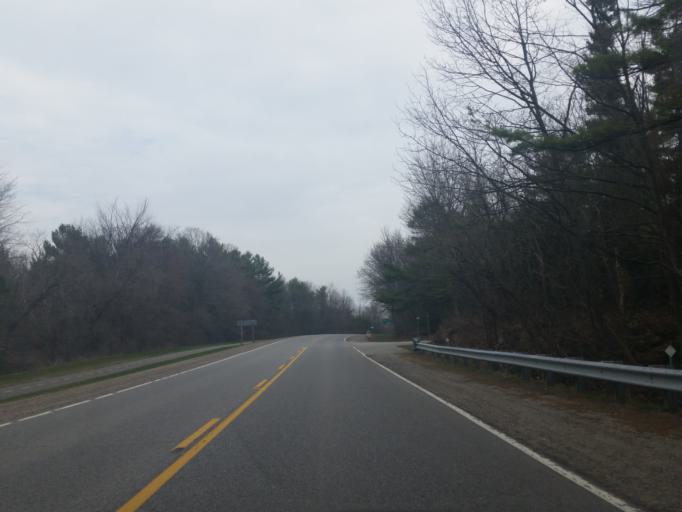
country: US
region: New York
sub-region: Jefferson County
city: Alexandria Bay
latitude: 44.3691
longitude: -75.9916
